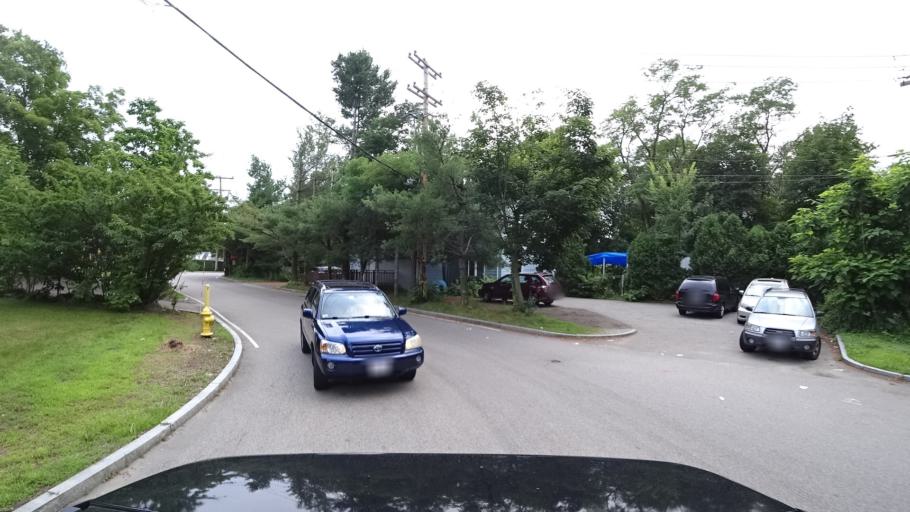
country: US
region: Massachusetts
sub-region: Norfolk County
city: Dedham
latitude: 42.2557
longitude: -71.1651
